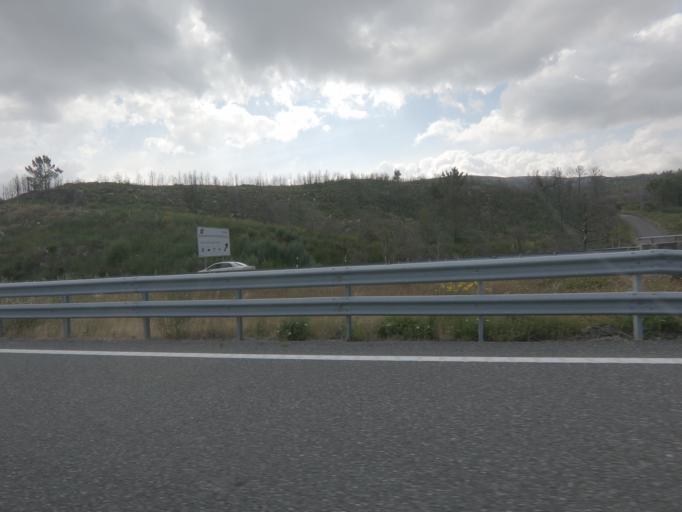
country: ES
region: Galicia
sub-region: Provincia de Ourense
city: Melon
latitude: 42.2730
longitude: -8.2032
